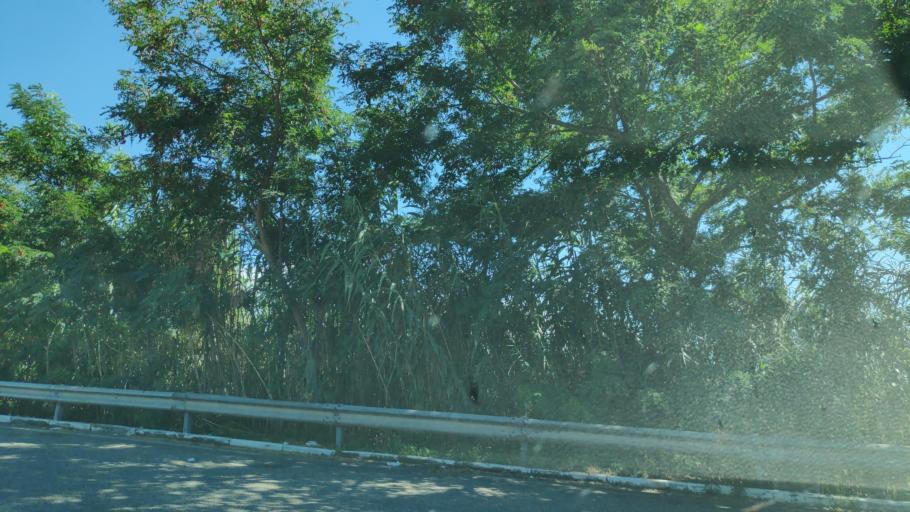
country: IT
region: Calabria
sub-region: Provincia di Catanzaro
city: Santa Eufemia Lamezia
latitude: 38.9292
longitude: 16.2365
